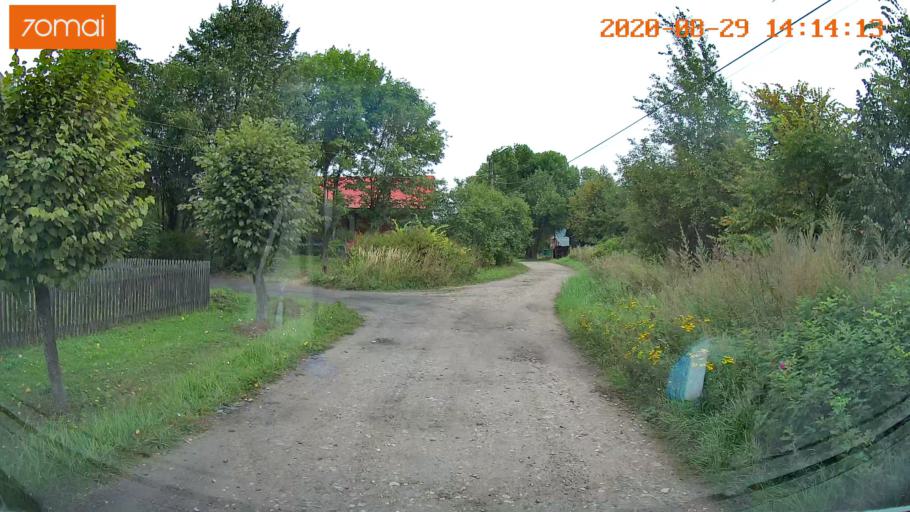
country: RU
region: Ivanovo
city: Yur'yevets
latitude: 57.3156
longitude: 43.1037
